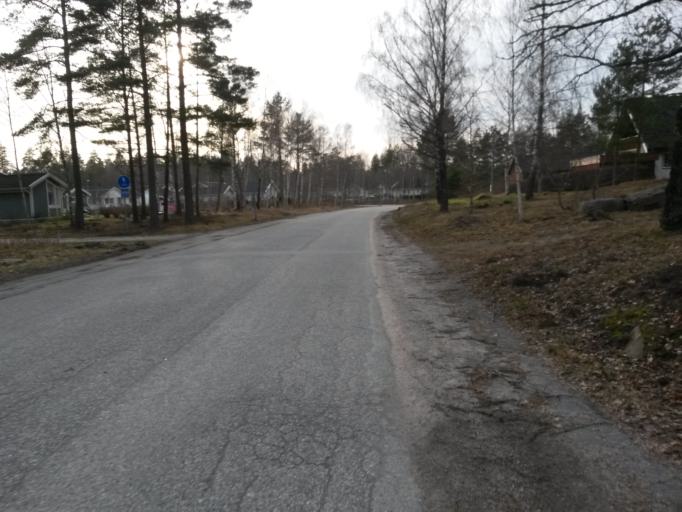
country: SE
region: Vaestra Goetaland
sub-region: Herrljunga Kommun
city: Herrljunga
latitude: 58.0680
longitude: 13.0309
